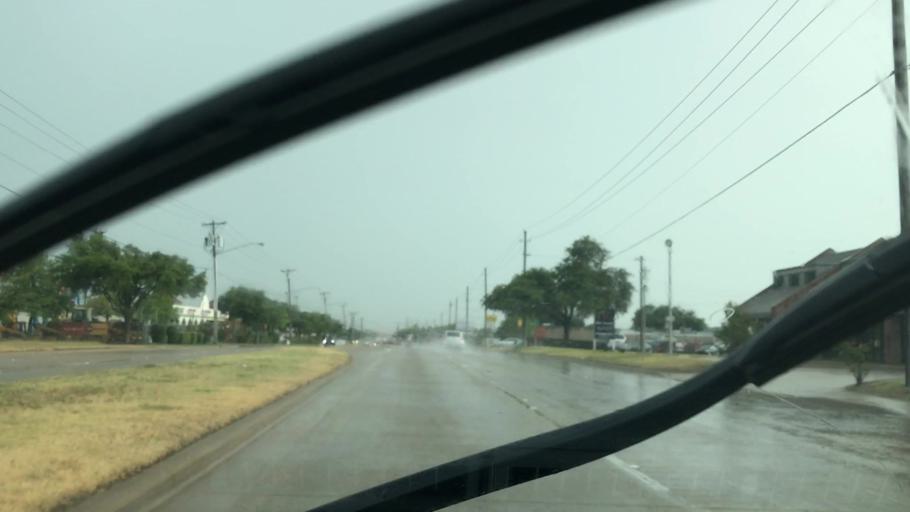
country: US
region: Texas
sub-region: Dallas County
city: Richardson
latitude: 32.8990
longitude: -96.7006
